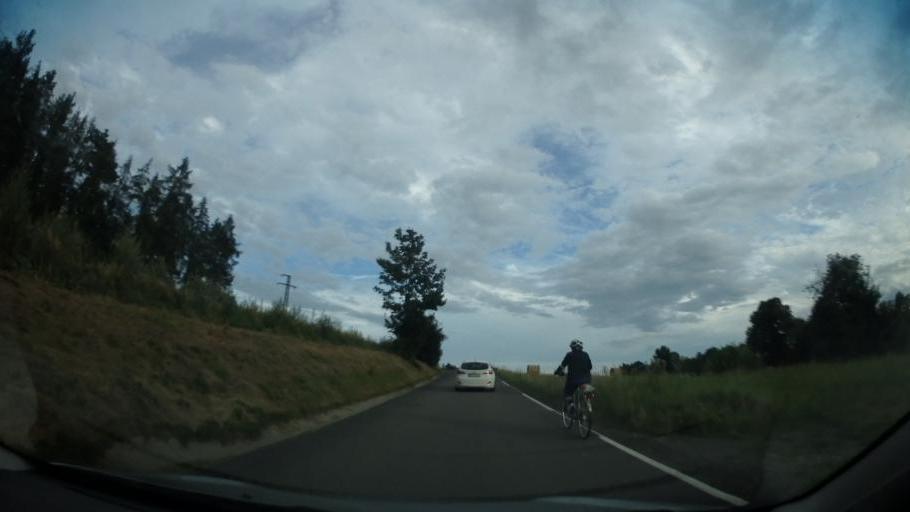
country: CZ
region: Olomoucky
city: Horni Stepanov
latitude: 49.5536
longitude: 16.7777
